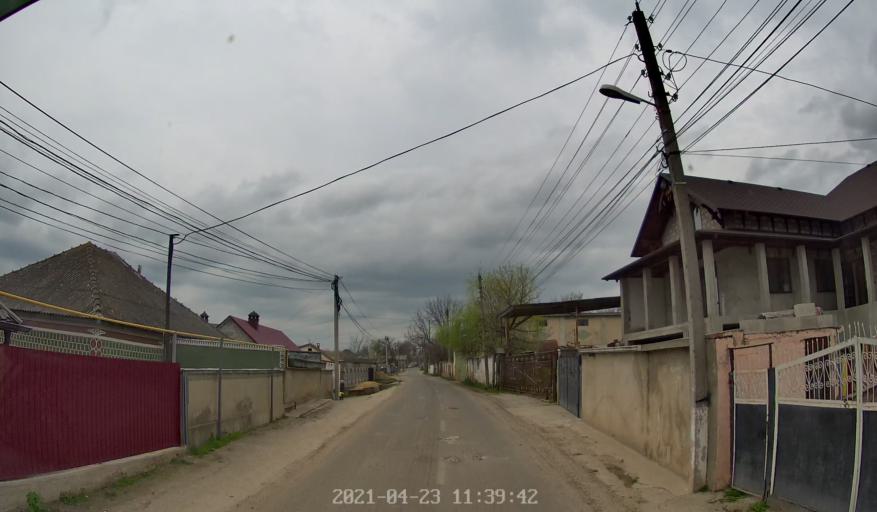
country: MD
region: Chisinau
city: Vadul lui Voda
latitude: 47.1179
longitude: 29.0530
